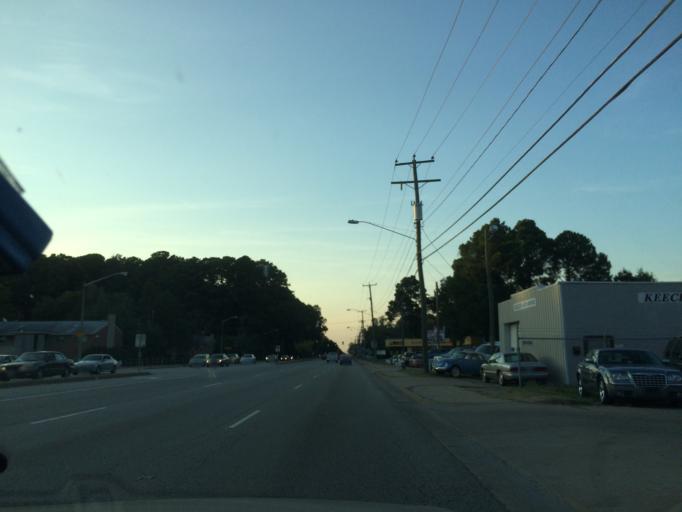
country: US
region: Virginia
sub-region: City of Newport News
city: Newport News
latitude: 37.0675
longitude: -76.4708
